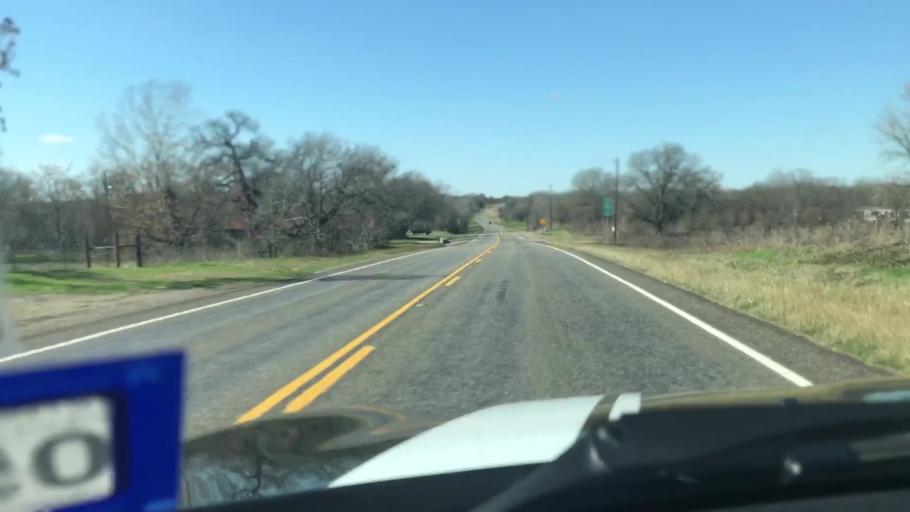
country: US
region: Texas
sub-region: Robertson County
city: Calvert
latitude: 30.8848
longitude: -96.7569
